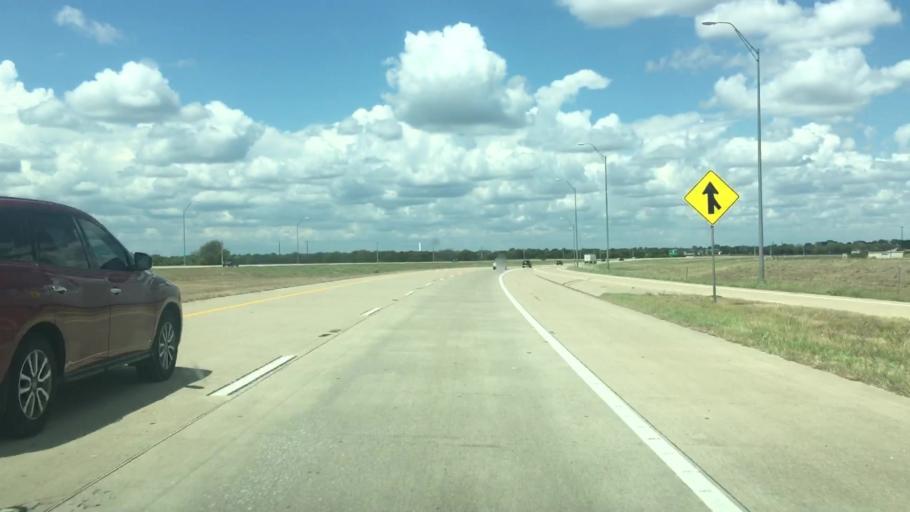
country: US
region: Texas
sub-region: Williamson County
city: Georgetown
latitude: 30.6251
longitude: -97.6231
